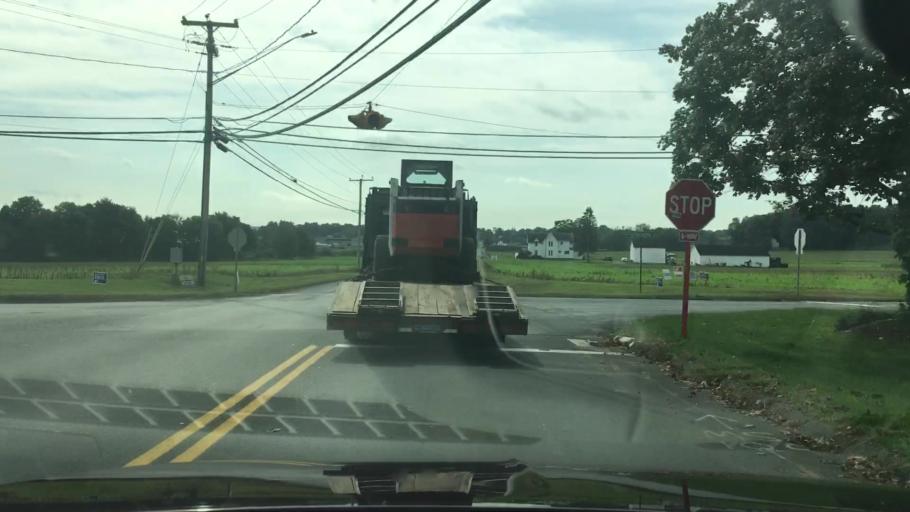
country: US
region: Connecticut
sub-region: Tolland County
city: Ellington
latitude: 41.9175
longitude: -72.4753
